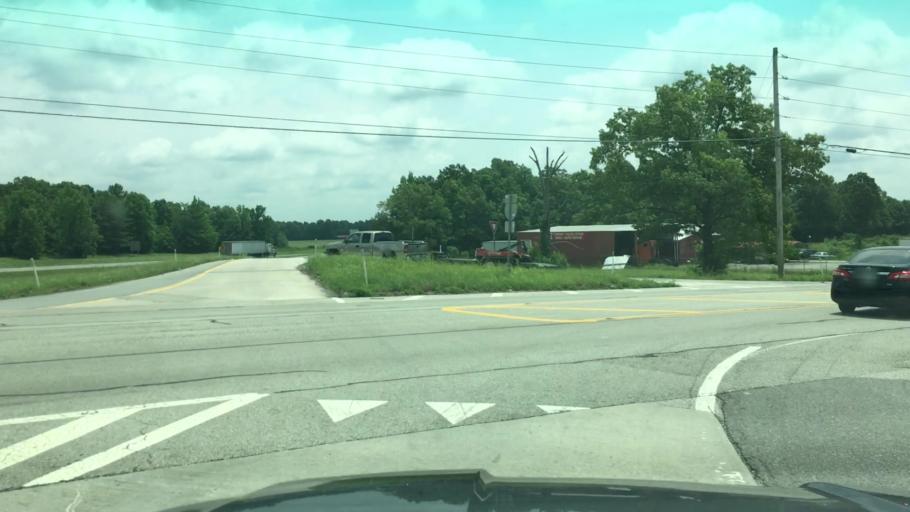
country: US
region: Tennessee
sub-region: Coffee County
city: New Union
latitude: 35.5336
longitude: -86.1624
